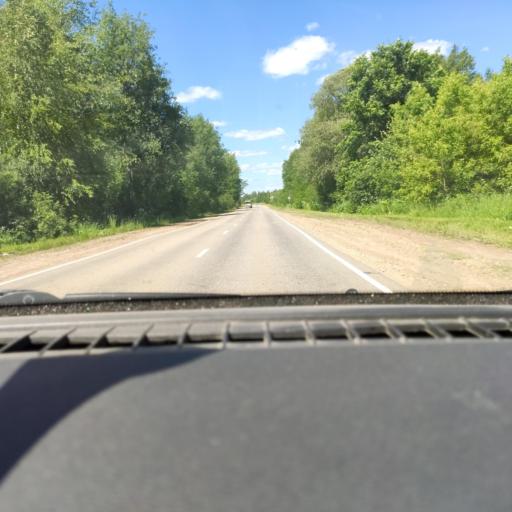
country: RU
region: Perm
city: Chaykovskaya
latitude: 58.0858
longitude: 55.6137
